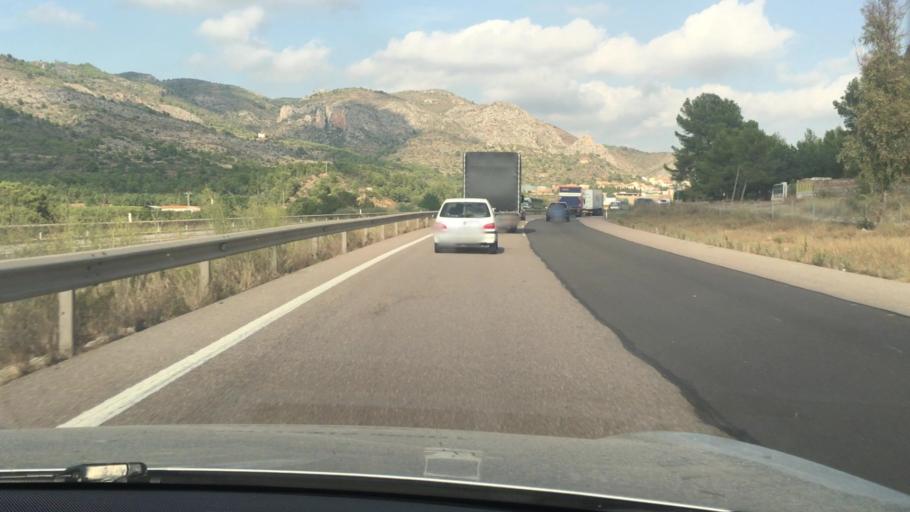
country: ES
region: Valencia
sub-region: Provincia de Castello
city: Borriol
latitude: 40.0284
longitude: -0.0872
